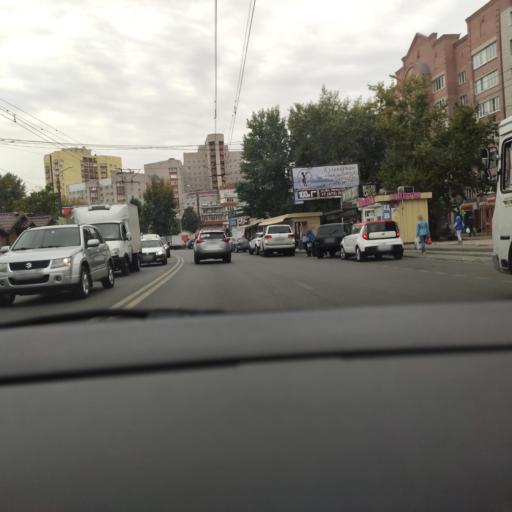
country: RU
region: Voronezj
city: Podgornoye
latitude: 51.7087
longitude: 39.1491
